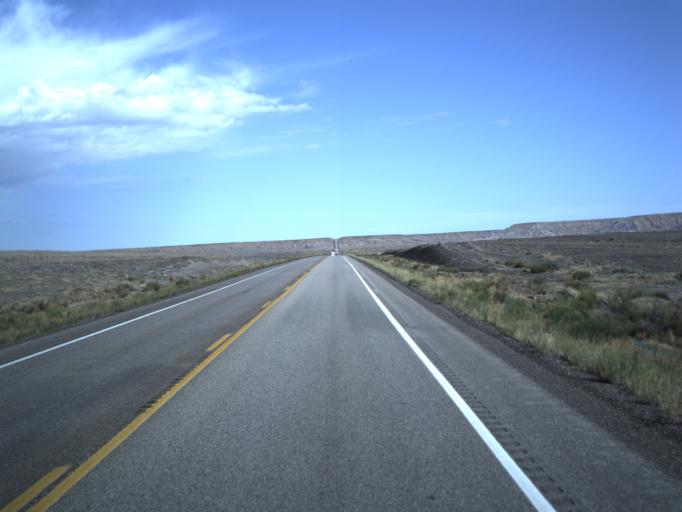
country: US
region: Utah
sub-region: Carbon County
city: East Carbon City
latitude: 39.3561
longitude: -110.3848
